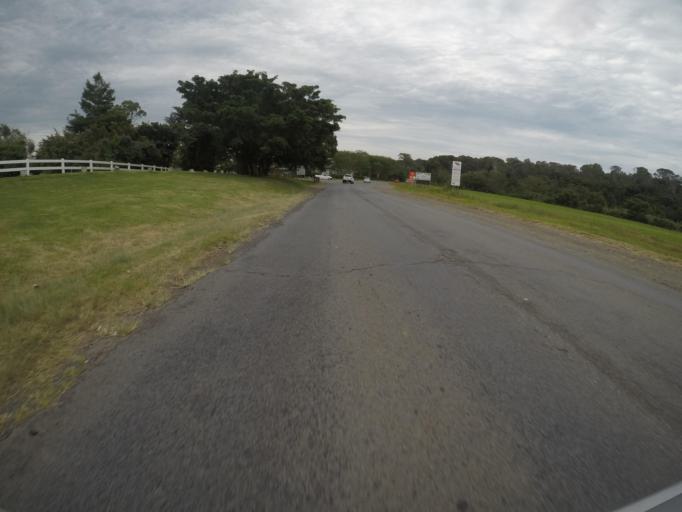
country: ZA
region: Eastern Cape
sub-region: Buffalo City Metropolitan Municipality
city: East London
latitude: -32.9395
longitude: 27.9393
